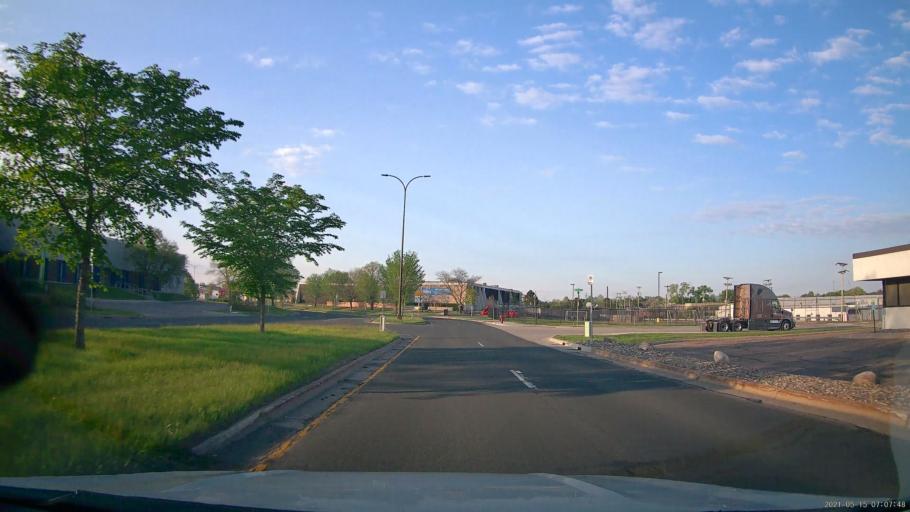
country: US
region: Minnesota
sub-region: Ramsey County
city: Lauderdale
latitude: 44.9937
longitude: -93.2117
